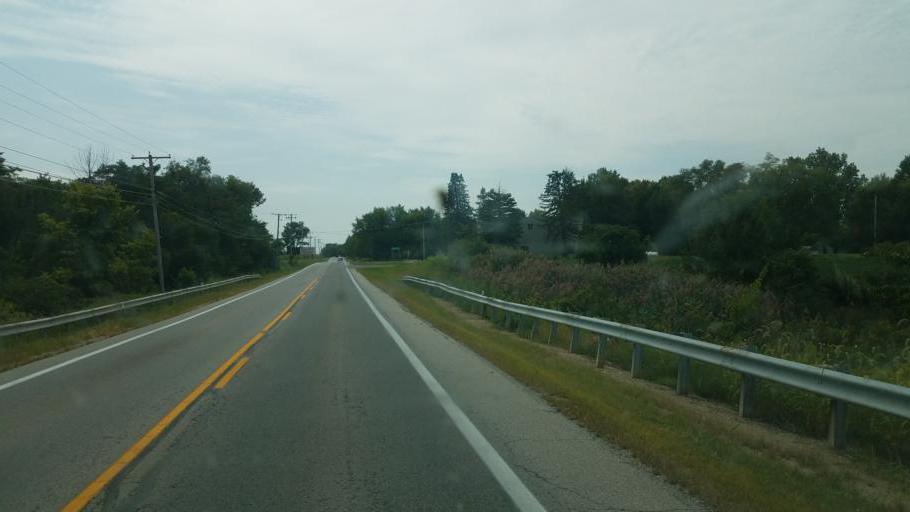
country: US
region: Ohio
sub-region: Marion County
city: Marion
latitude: 40.5143
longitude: -83.0982
